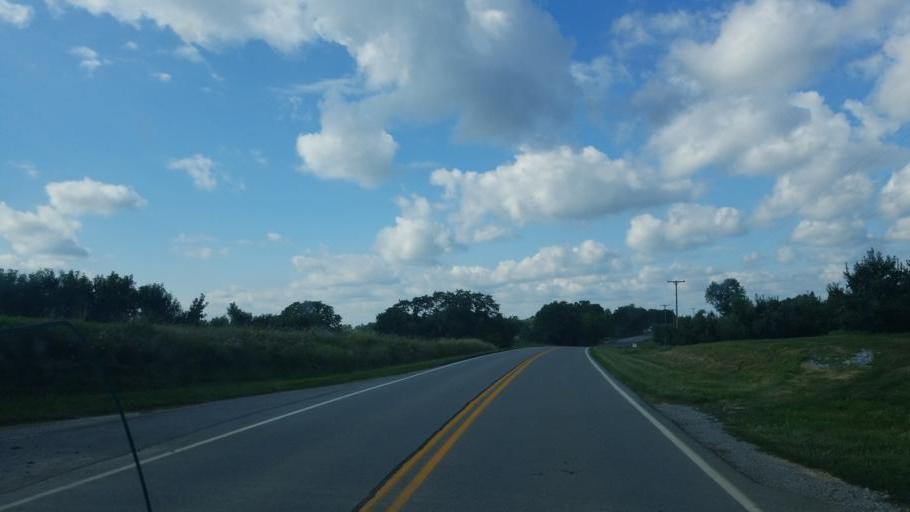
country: US
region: Illinois
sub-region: Union County
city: Cobden
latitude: 37.5904
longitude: -89.3239
